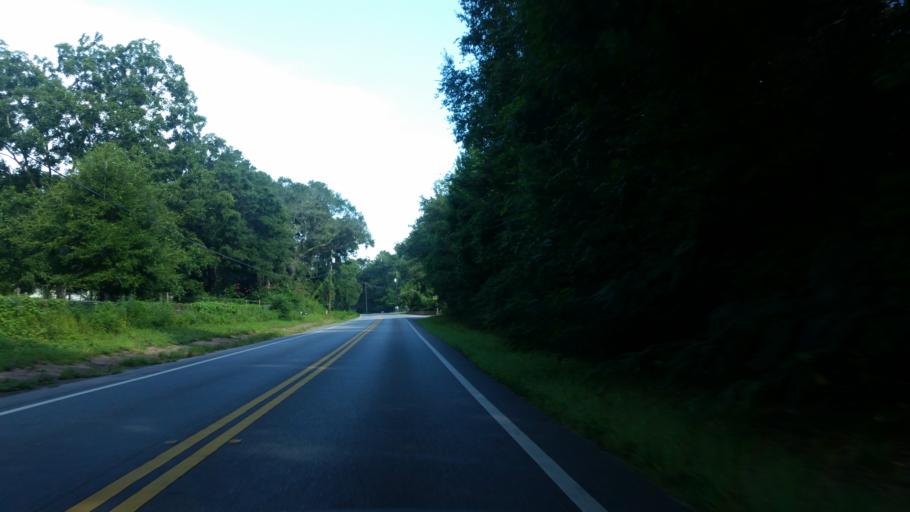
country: US
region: Florida
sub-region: Santa Rosa County
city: Milton
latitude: 30.6222
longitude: -87.0988
